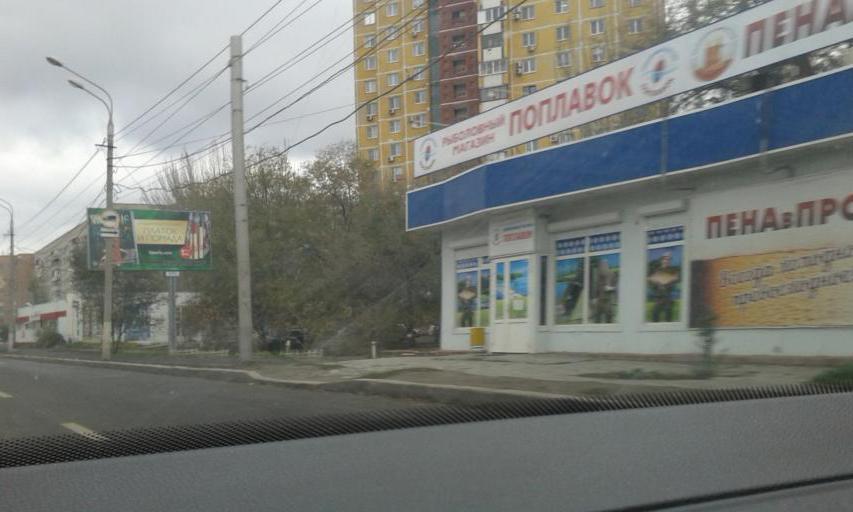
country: RU
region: Volgograd
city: Volgograd
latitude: 48.7214
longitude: 44.5100
